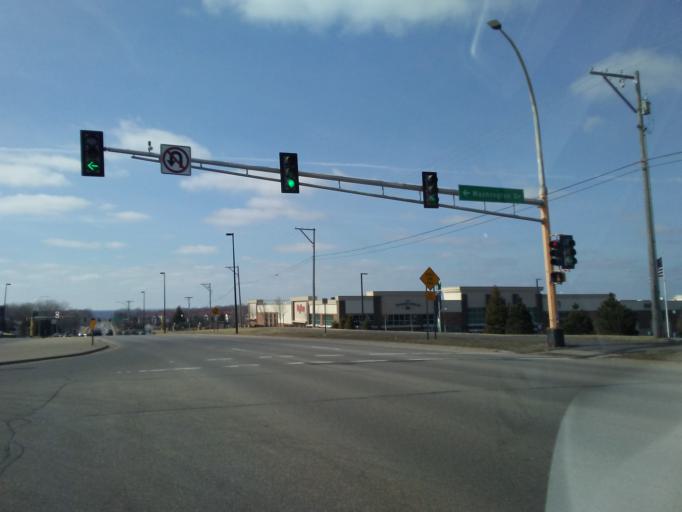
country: US
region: Minnesota
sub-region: Dakota County
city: Eagan
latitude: 44.8336
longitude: -93.1695
